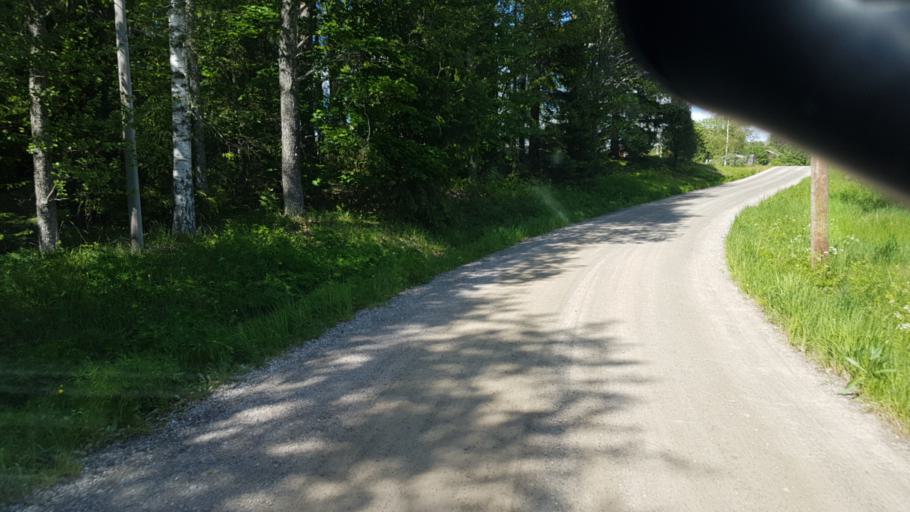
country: SE
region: Vaermland
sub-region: Karlstads Kommun
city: Edsvalla
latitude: 59.6049
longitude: 12.9179
